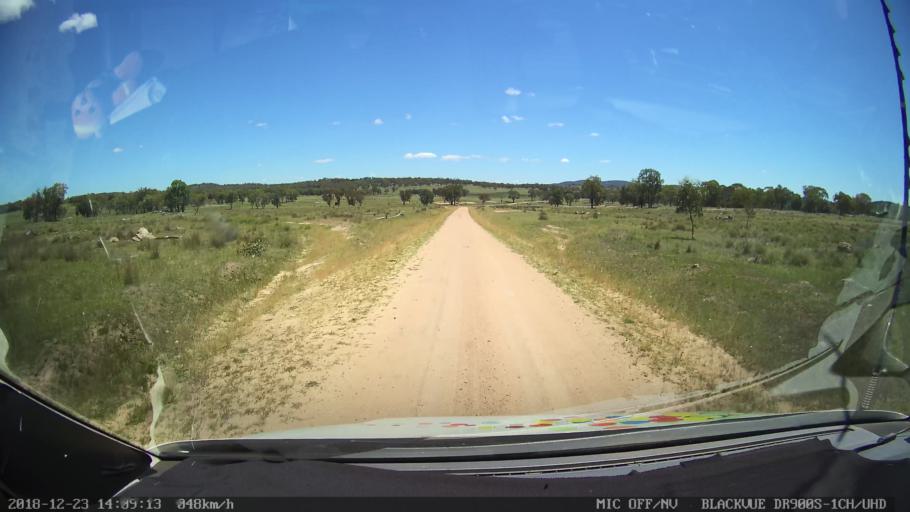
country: AU
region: New South Wales
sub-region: Tamworth Municipality
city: Manilla
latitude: -30.6438
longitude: 151.0636
